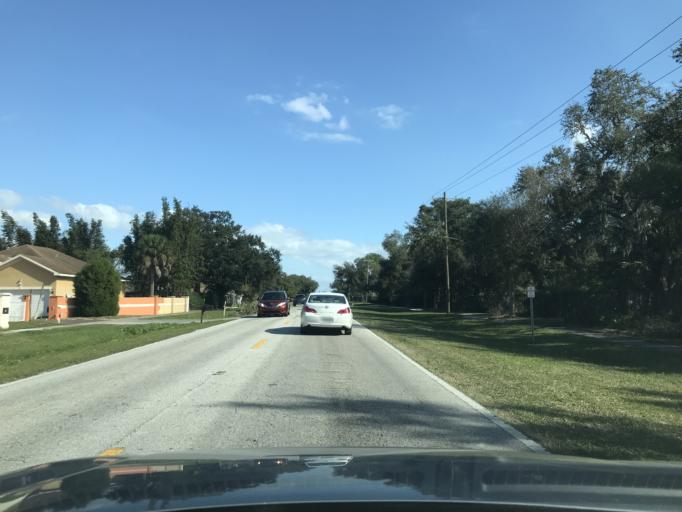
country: US
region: Florida
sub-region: Pinellas County
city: Largo
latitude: 27.9387
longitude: -82.7666
